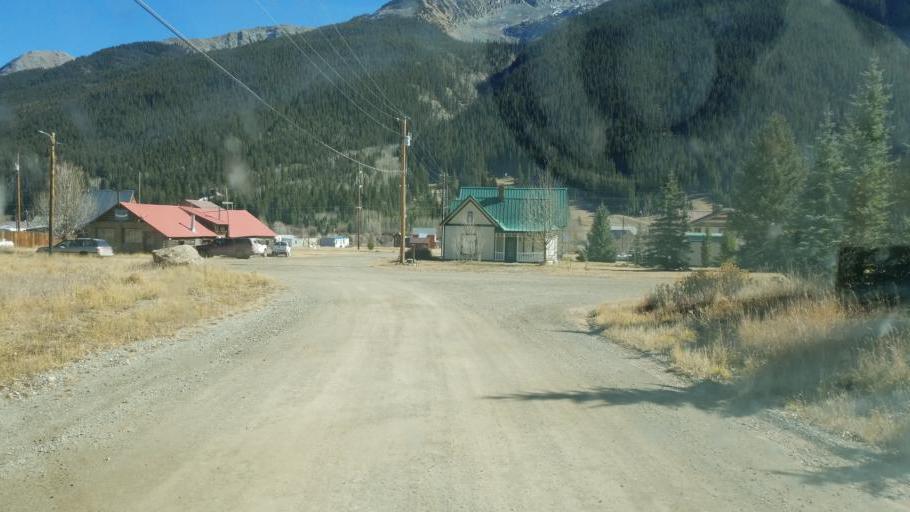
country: US
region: Colorado
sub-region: San Juan County
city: Silverton
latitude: 37.8154
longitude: -107.6602
